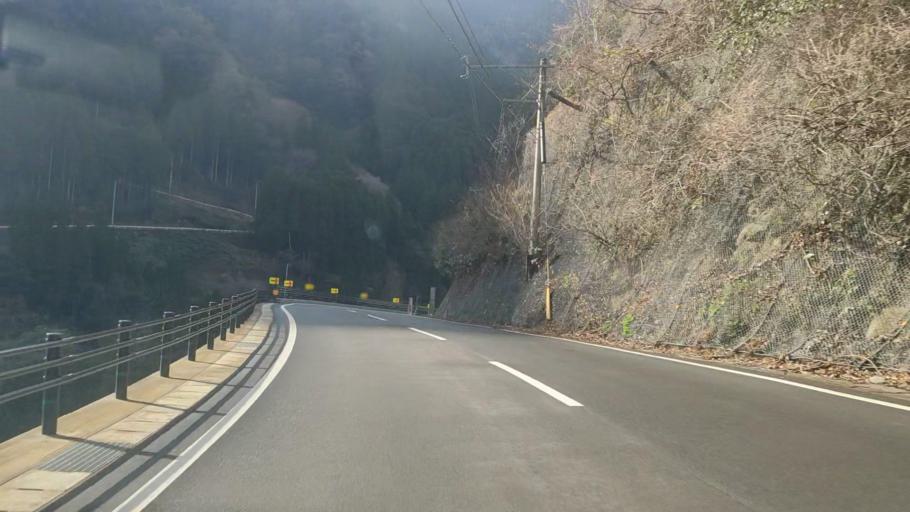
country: JP
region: Kumamoto
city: Hitoyoshi
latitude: 32.4128
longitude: 130.8426
